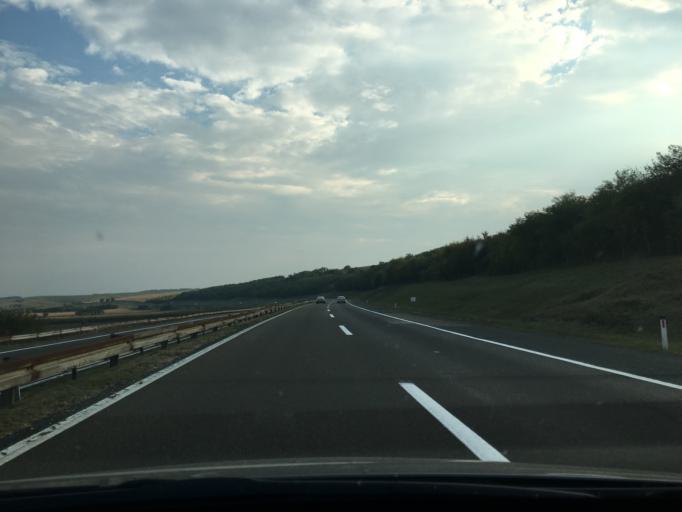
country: RS
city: Lugavcina
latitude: 44.4988
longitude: 21.0232
